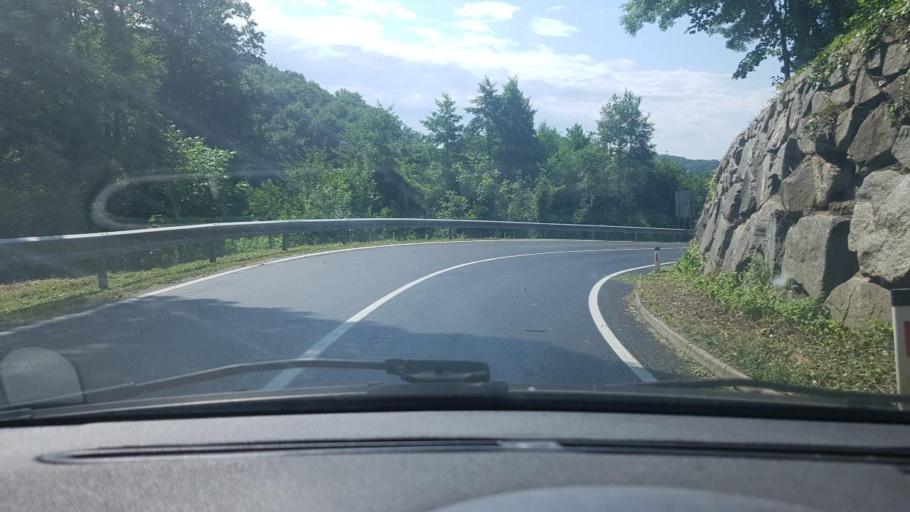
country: SI
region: Sentilj
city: Sentilj v Slov. Goricah
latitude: 46.6845
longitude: 15.6550
